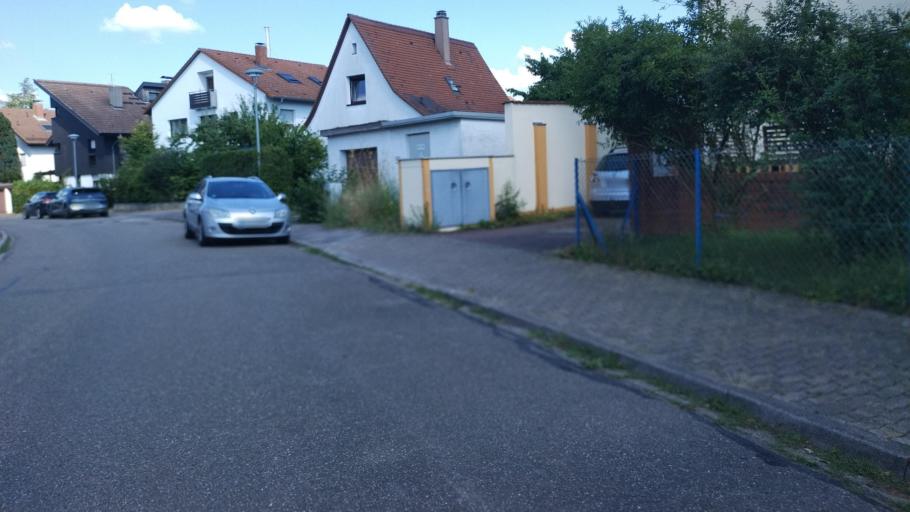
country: DE
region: Baden-Wuerttemberg
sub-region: Karlsruhe Region
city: Ettlingen
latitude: 48.9654
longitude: 8.3977
